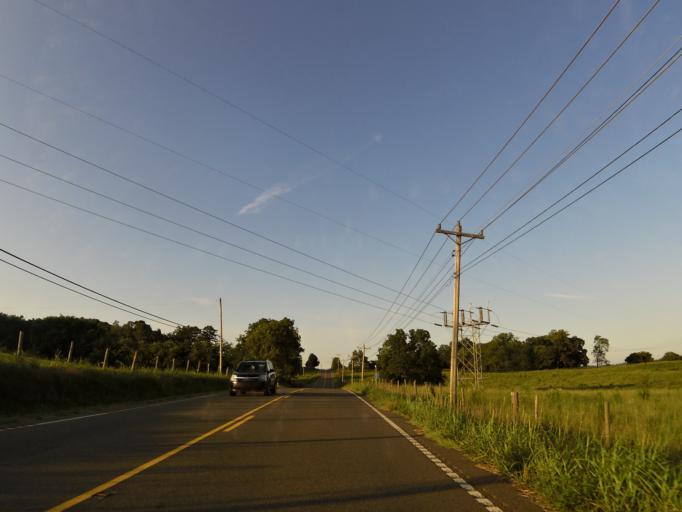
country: US
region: Tennessee
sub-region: Meigs County
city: Decatur
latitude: 35.6296
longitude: -84.6960
